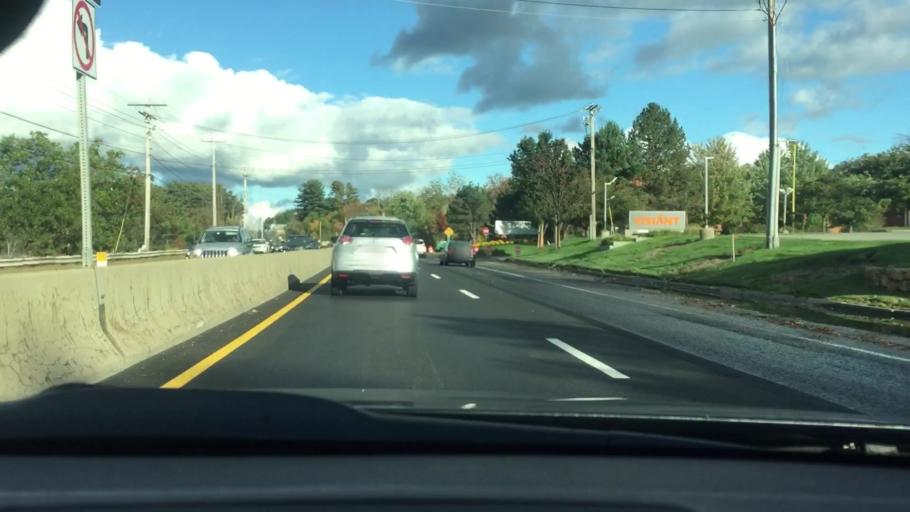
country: US
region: Massachusetts
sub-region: Worcester County
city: Southborough
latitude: 42.2928
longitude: -71.5161
